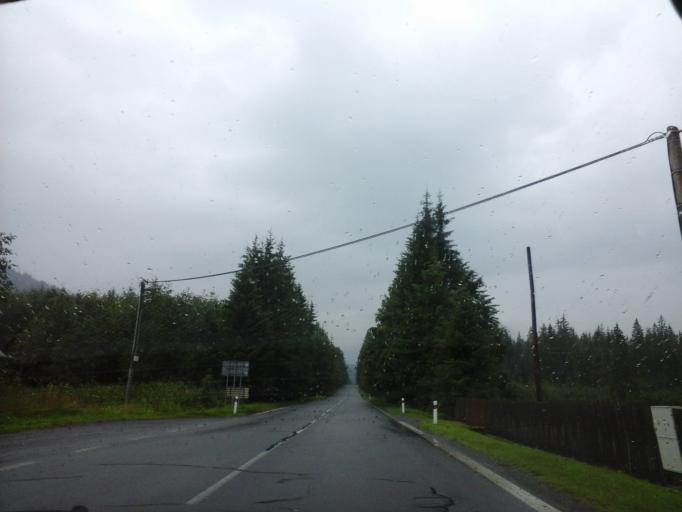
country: SK
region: Presovsky
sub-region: Okres Poprad
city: Zdiar
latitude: 49.2802
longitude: 20.1741
